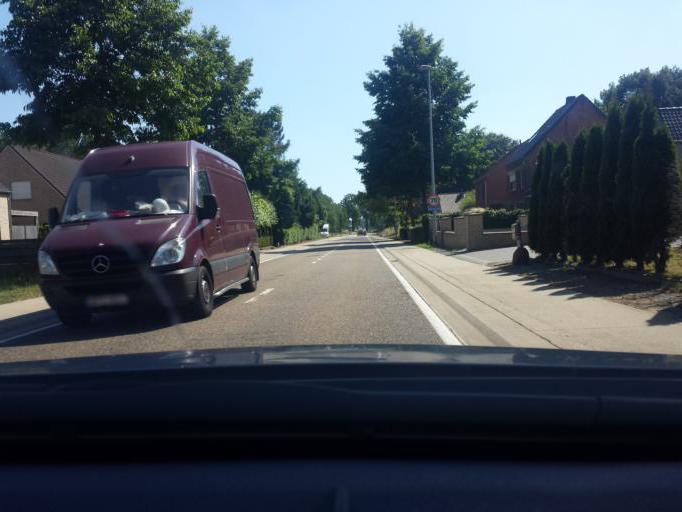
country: BE
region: Flanders
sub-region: Provincie Limburg
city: Beringen
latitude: 51.0362
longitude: 5.2134
